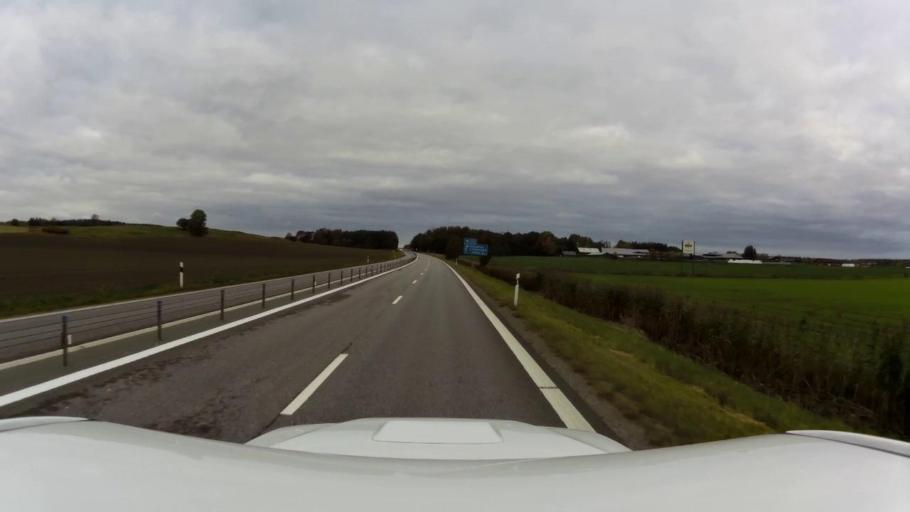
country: SE
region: OEstergoetland
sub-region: Linkopings Kommun
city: Ljungsbro
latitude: 58.4819
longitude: 15.4833
